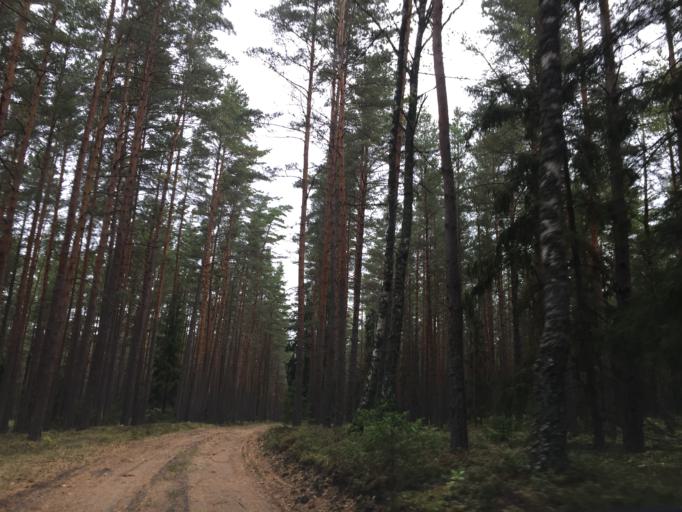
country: LV
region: Salacgrivas
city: Salacgriva
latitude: 57.7073
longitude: 24.3536
